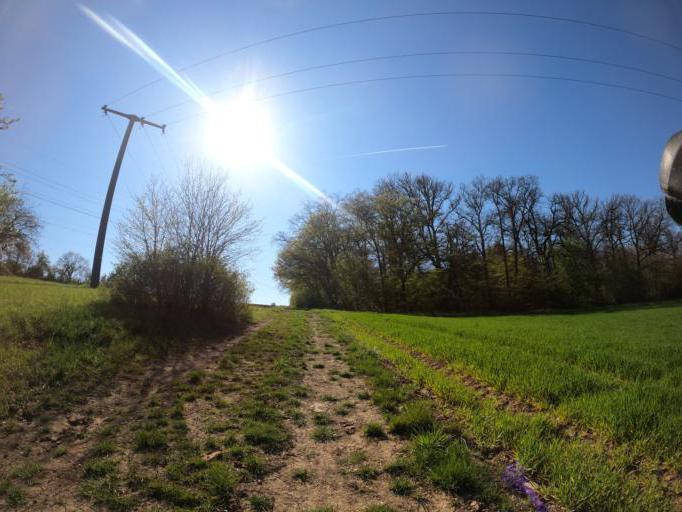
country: DE
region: Baden-Wuerttemberg
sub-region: Karlsruhe Region
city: Monsheim
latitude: 48.8978
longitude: 8.8874
